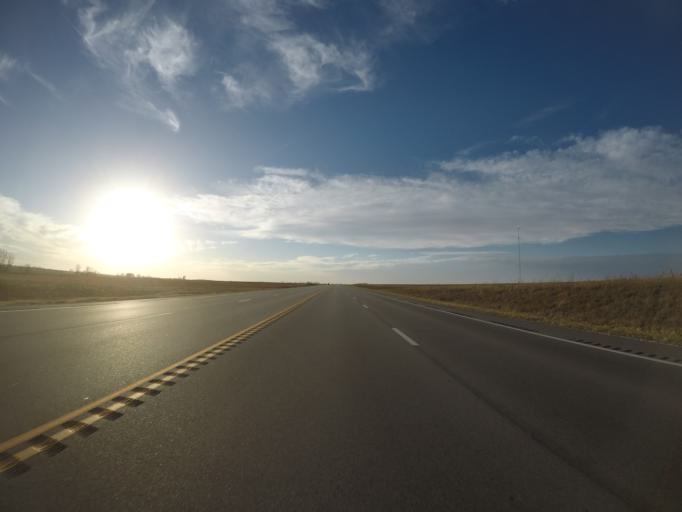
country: US
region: Kansas
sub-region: Chase County
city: Cottonwood Falls
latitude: 38.4052
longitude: -96.4055
